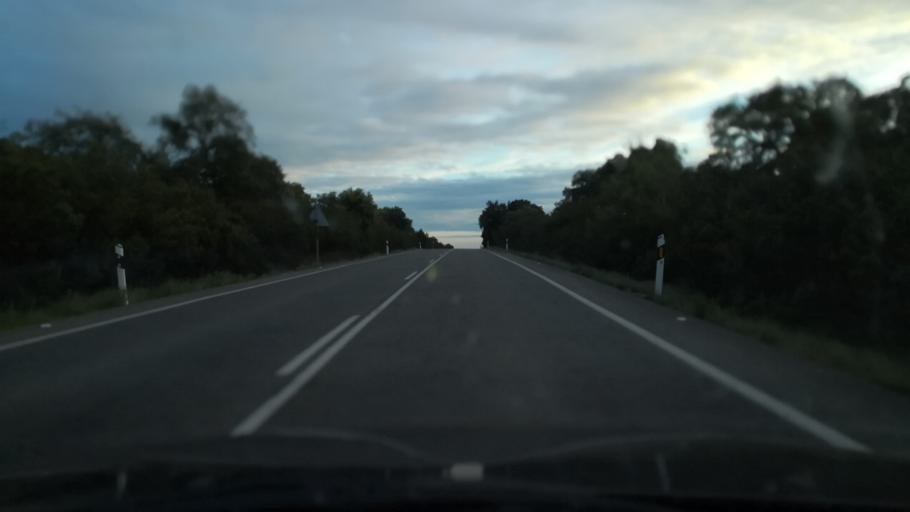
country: ES
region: Extremadura
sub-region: Provincia de Badajoz
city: Puebla de Obando
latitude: 39.1545
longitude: -6.6463
